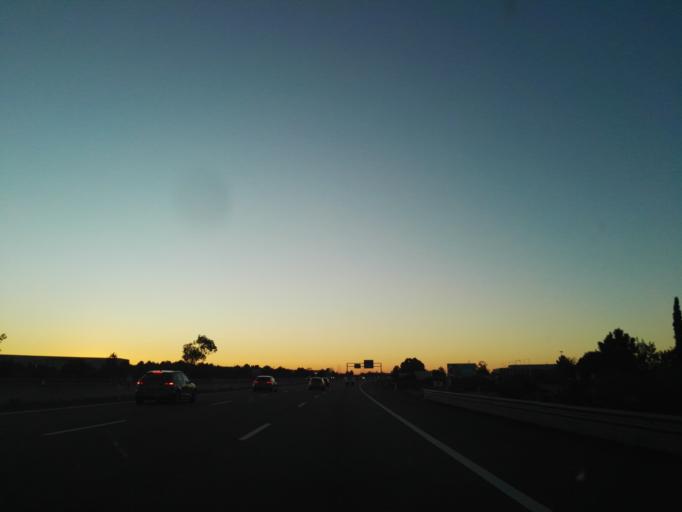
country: PT
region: Setubal
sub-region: Palmela
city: Quinta do Anjo
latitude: 38.5795
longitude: -8.9924
